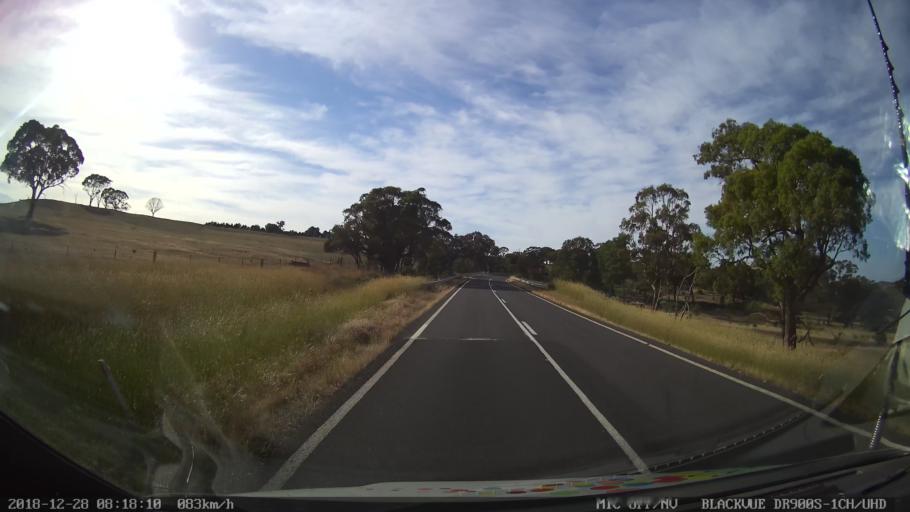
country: AU
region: New South Wales
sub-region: Blayney
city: Blayney
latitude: -33.8442
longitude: 149.3472
